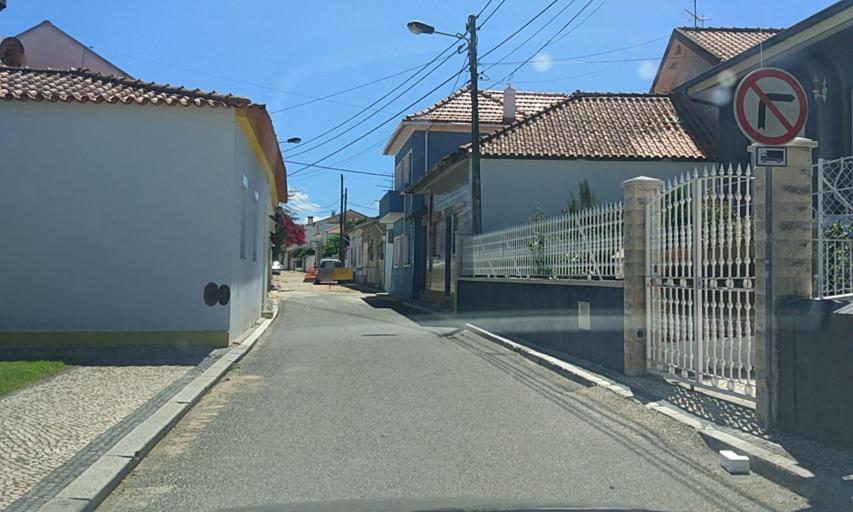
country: PT
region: Aveiro
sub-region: Ilhavo
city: Ilhavo
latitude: 40.6051
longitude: -8.6757
